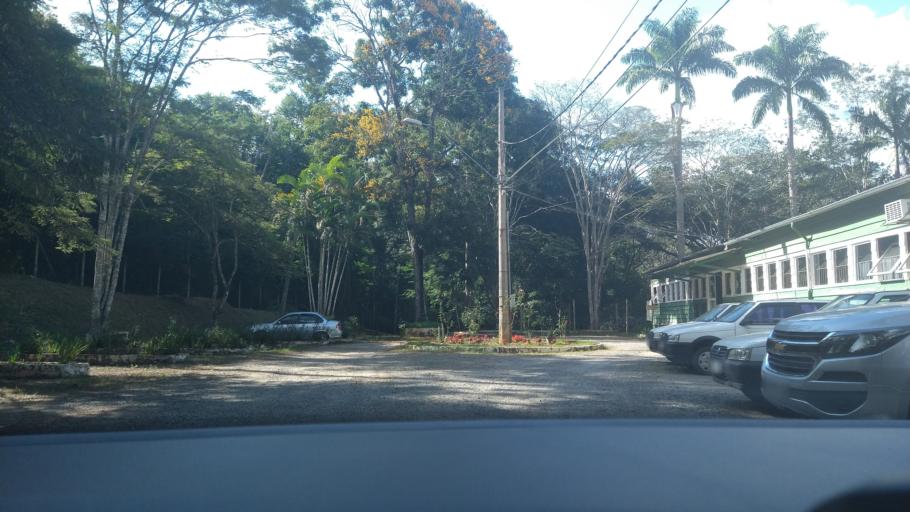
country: BR
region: Minas Gerais
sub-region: Vicosa
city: Vicosa
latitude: -20.7701
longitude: -42.8766
